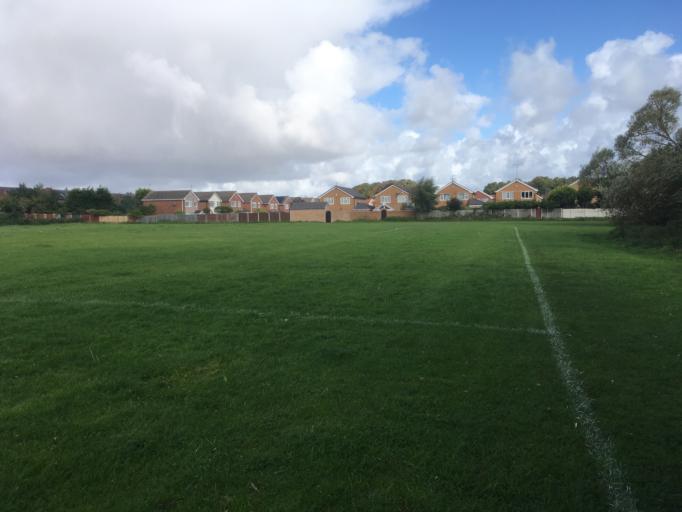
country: GB
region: England
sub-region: Sefton
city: Southport
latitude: 53.6522
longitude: -2.9620
